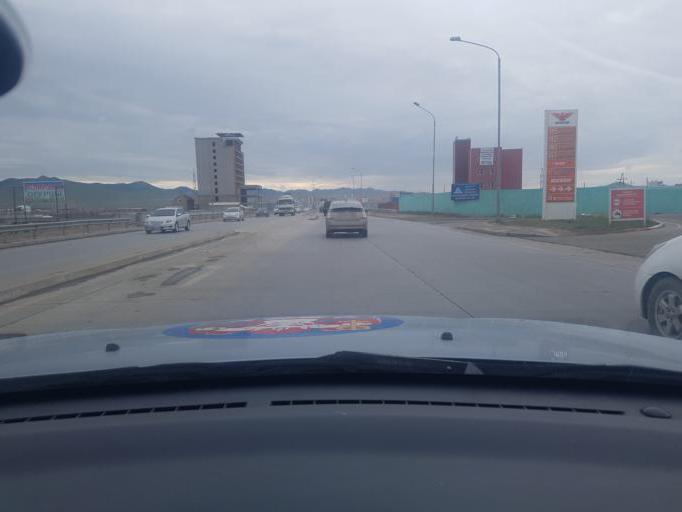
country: MN
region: Ulaanbaatar
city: Ulaanbaatar
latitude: 47.8946
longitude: 106.7854
